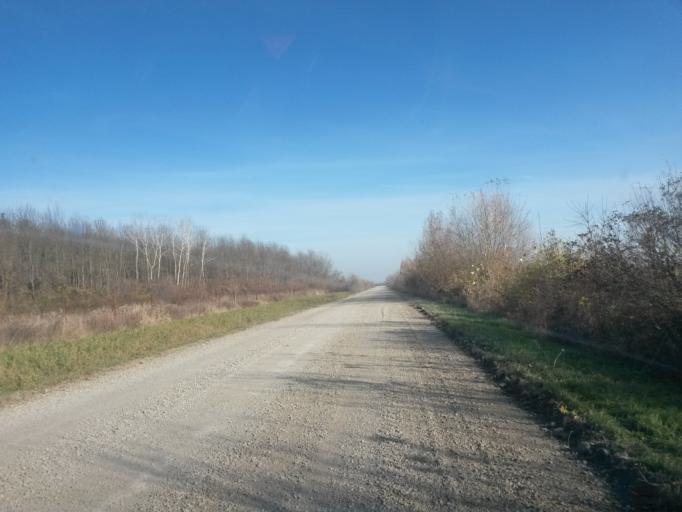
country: HR
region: Vukovarsko-Srijemska
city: Privlaka
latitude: 45.2196
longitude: 18.8622
